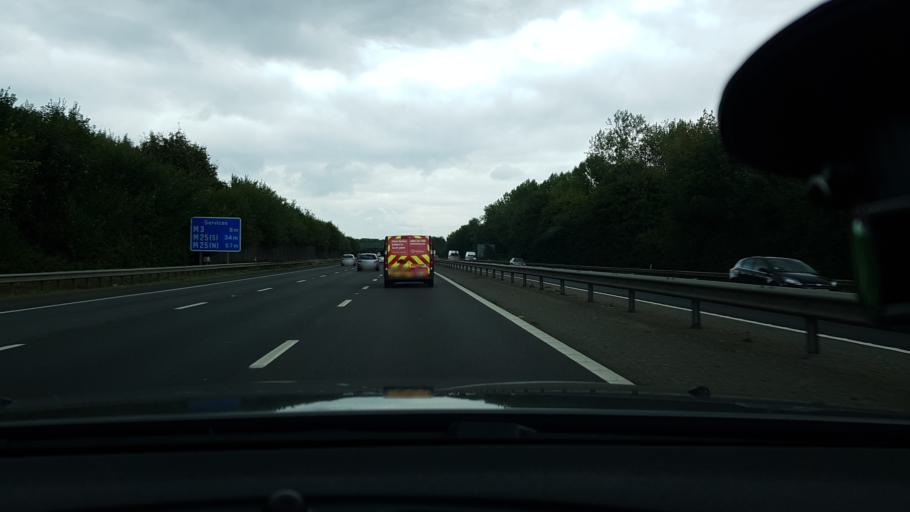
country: GB
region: England
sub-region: Hampshire
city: Old Basing
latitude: 51.2623
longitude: -1.0382
